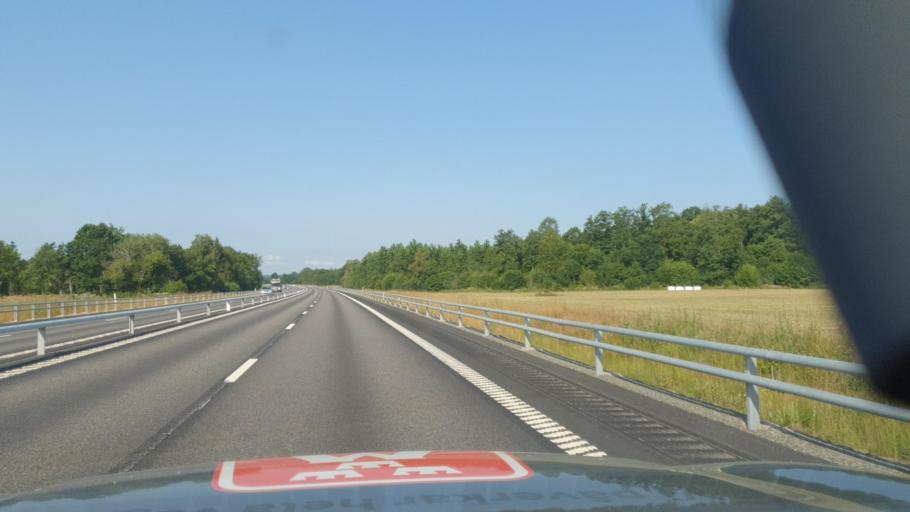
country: SE
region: Skane
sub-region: Kristianstads Kommun
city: Onnestad
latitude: 55.9609
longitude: 13.9543
